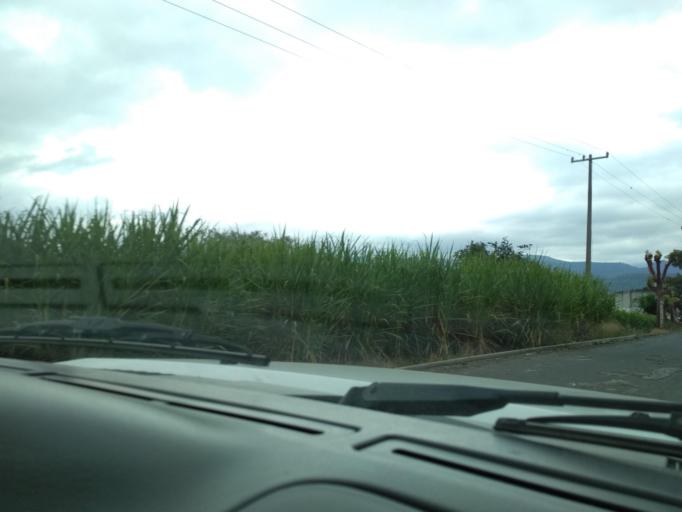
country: MX
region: Veracruz
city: El Castillo
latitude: 19.5828
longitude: -96.8237
